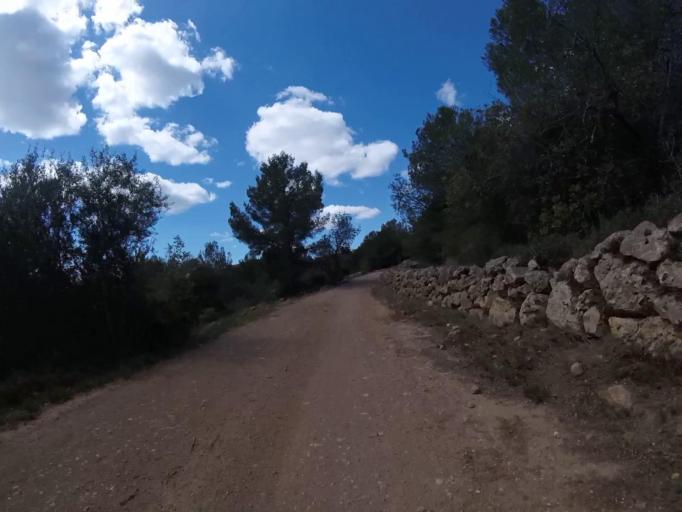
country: ES
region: Valencia
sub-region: Provincia de Castello
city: Santa Magdalena de Pulpis
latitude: 40.3209
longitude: 0.3327
